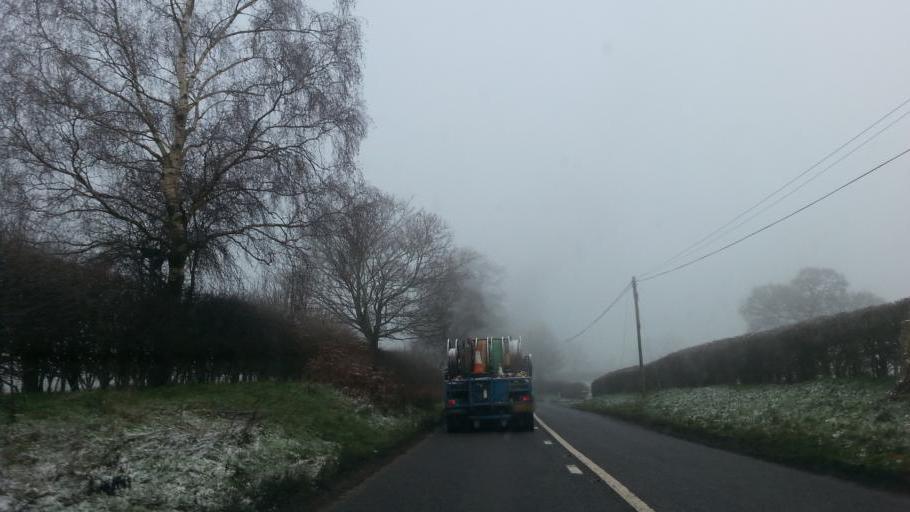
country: GB
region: England
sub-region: Cheshire East
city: Eaton
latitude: 53.2018
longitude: -2.2248
